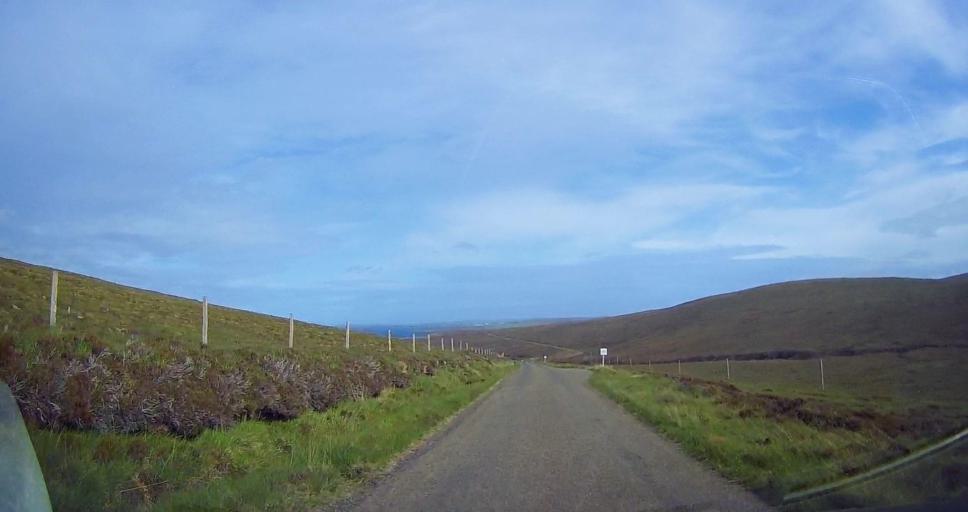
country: GB
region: Scotland
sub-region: Orkney Islands
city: Stromness
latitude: 58.8752
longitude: -3.2459
